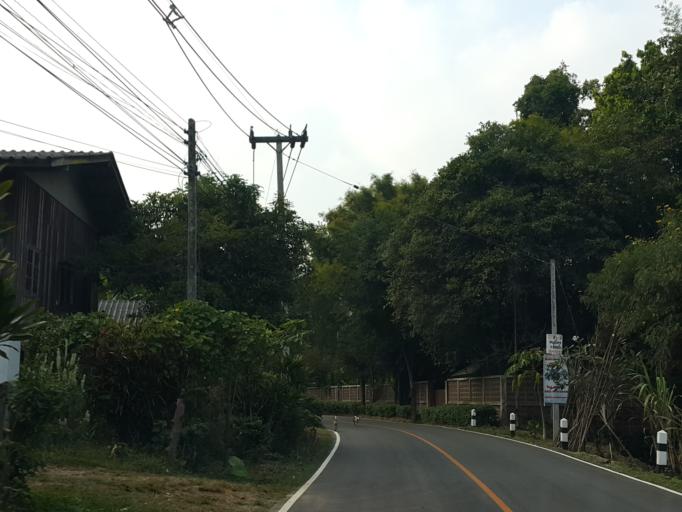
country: TH
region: Chiang Mai
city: Mae On
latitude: 18.9077
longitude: 99.2513
